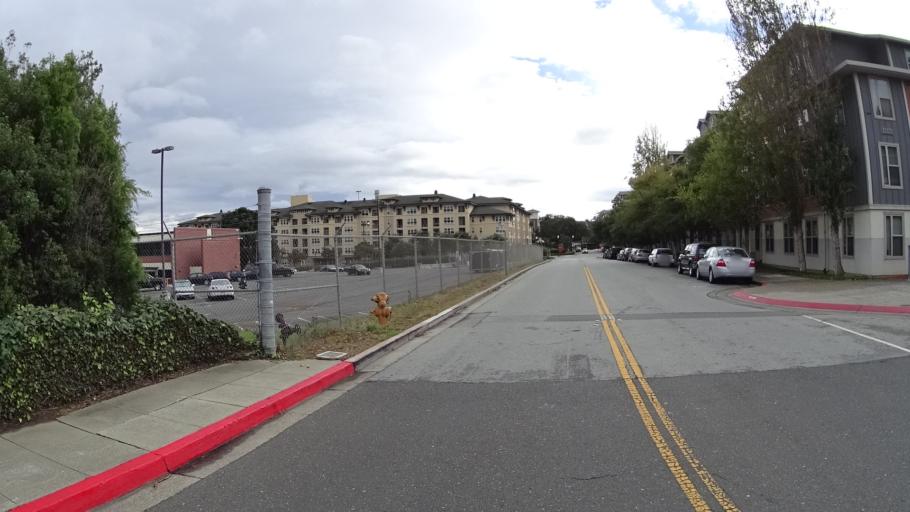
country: US
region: California
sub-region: San Mateo County
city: San Bruno
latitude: 37.6354
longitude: -122.4233
